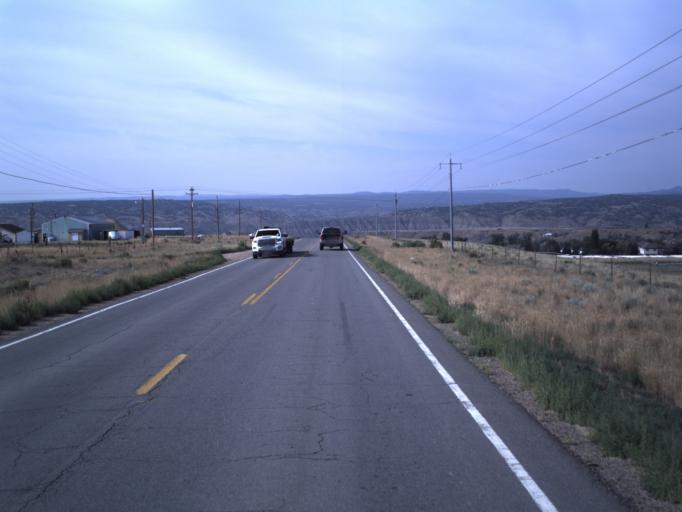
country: US
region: Utah
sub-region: Duchesne County
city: Duchesne
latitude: 40.1871
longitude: -110.3957
